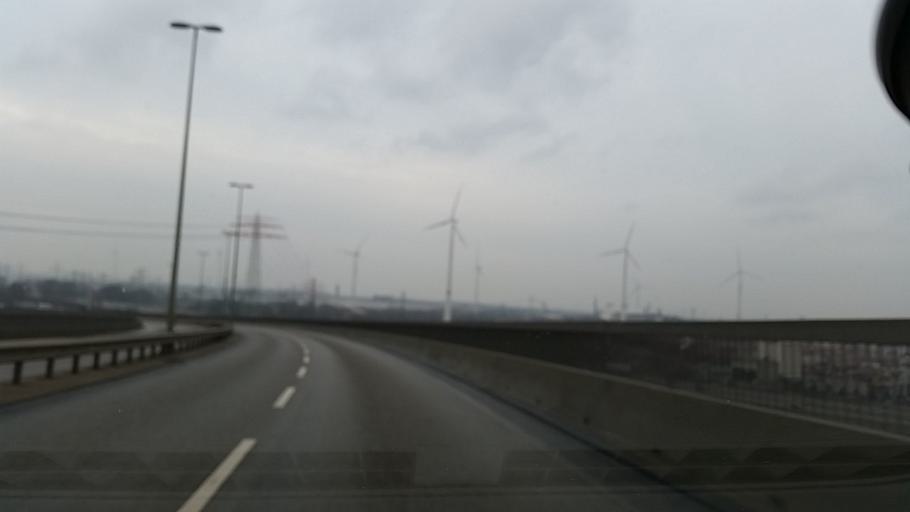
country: DE
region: Hamburg
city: Altona
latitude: 53.5223
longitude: 9.9321
